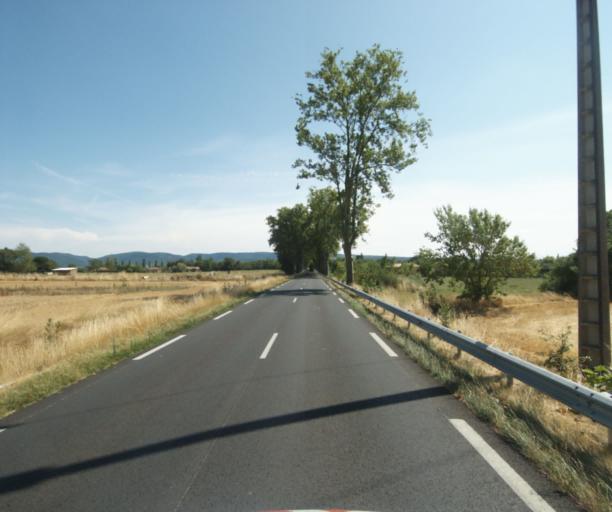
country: FR
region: Midi-Pyrenees
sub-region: Departement de la Haute-Garonne
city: Revel
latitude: 43.4916
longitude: 2.0132
